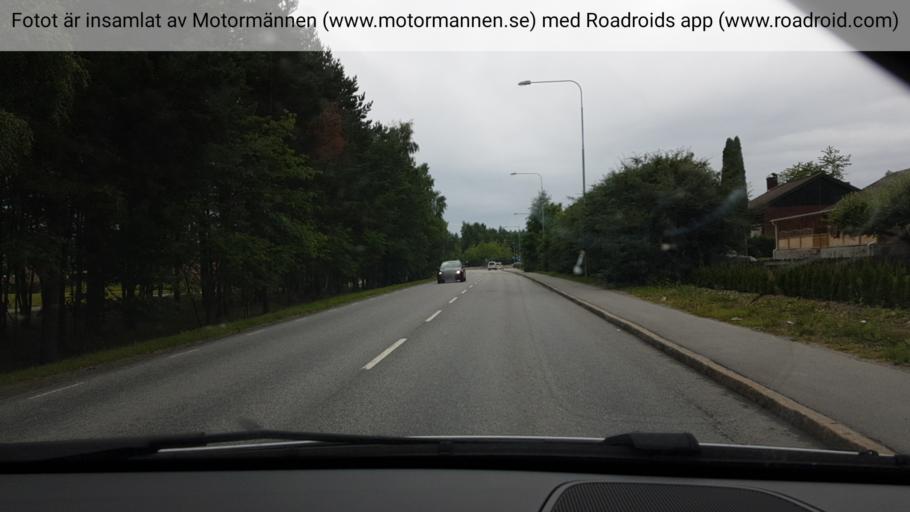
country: SE
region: Stockholm
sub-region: Sodertalje Kommun
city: Soedertaelje
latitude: 59.2012
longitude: 17.5994
